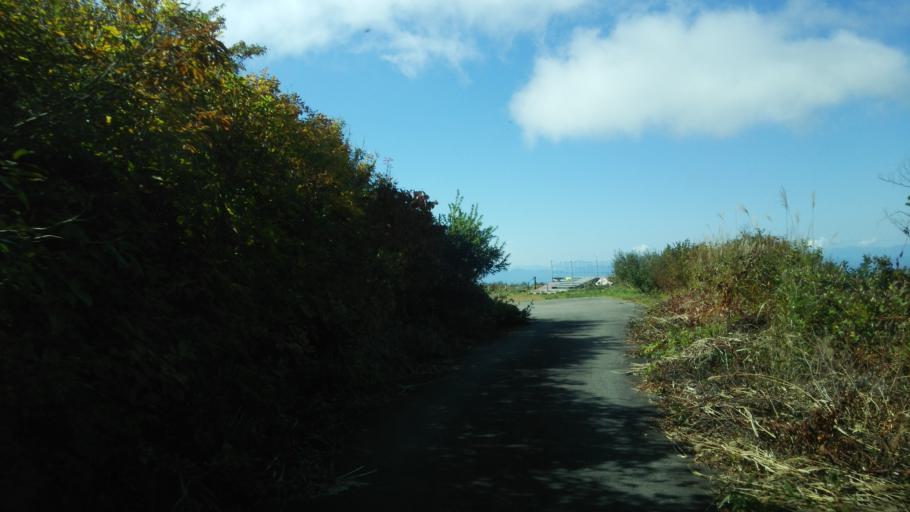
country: JP
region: Fukushima
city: Kitakata
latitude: 37.6184
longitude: 139.9944
